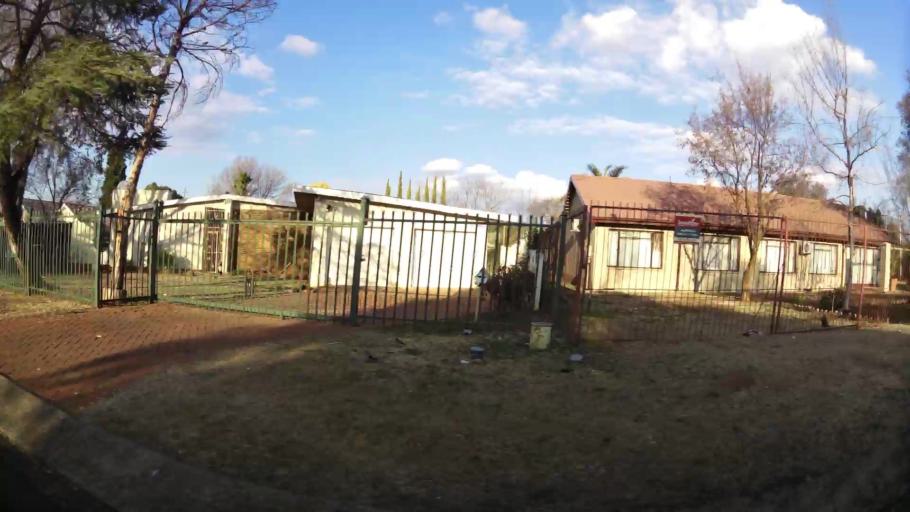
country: ZA
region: Orange Free State
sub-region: Mangaung Metropolitan Municipality
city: Bloemfontein
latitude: -29.1519
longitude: 26.1863
